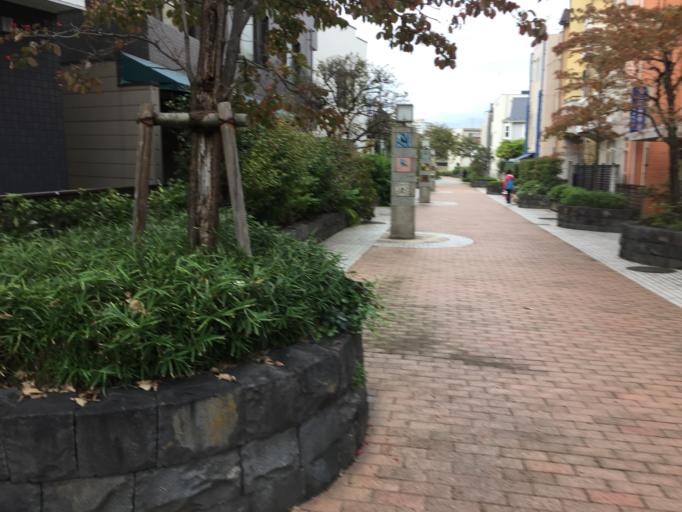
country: JP
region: Tokyo
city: Tokyo
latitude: 35.6491
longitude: 139.6724
